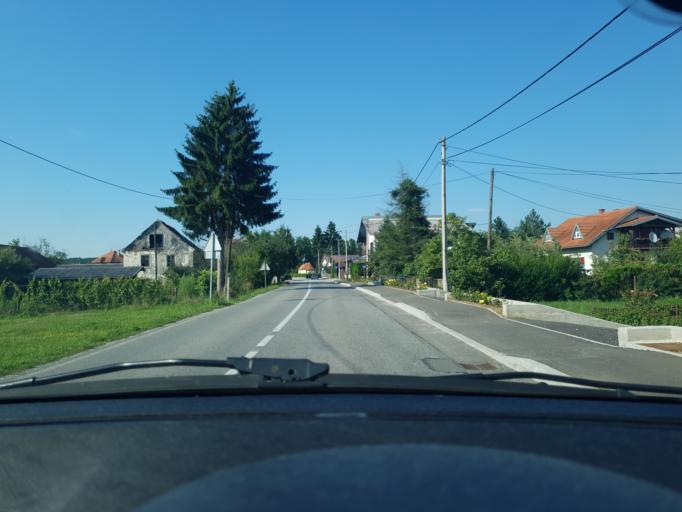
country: HR
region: Zagrebacka
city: Jablanovec
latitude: 45.9021
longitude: 15.8528
